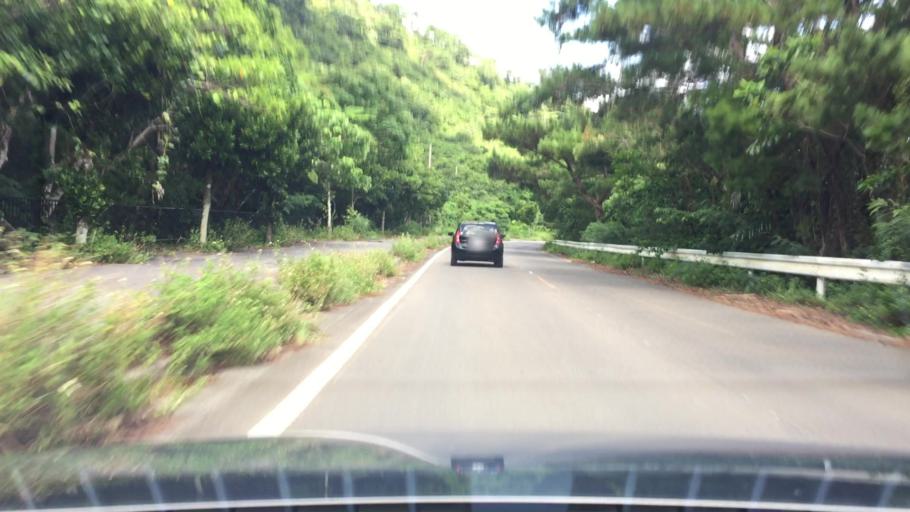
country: JP
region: Okinawa
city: Ishigaki
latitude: 24.4500
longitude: 124.2081
